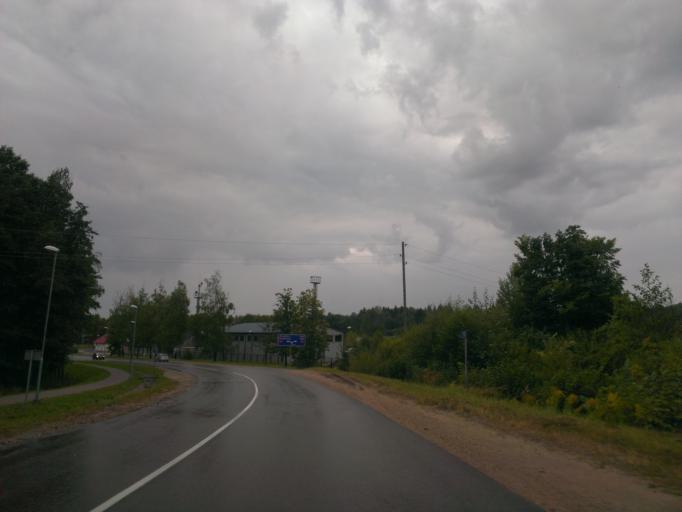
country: LV
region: Kegums
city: Kegums
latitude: 56.7492
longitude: 24.7221
